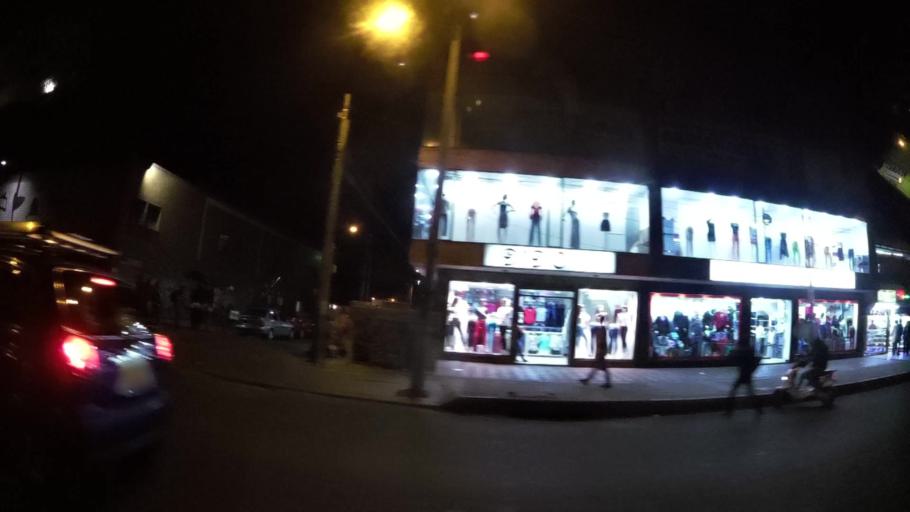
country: CO
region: Bogota D.C.
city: Bogota
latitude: 4.6235
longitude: -74.1494
